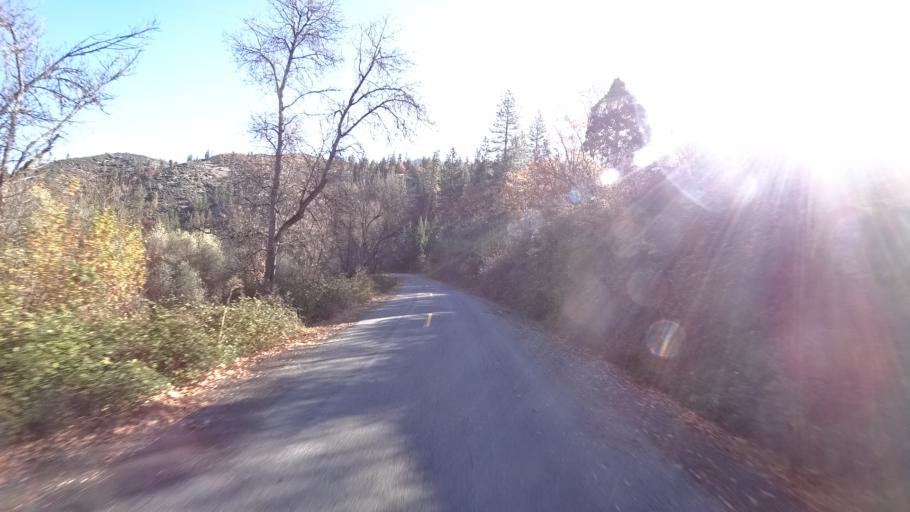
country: US
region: California
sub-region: Siskiyou County
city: Yreka
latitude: 41.8221
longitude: -122.9645
